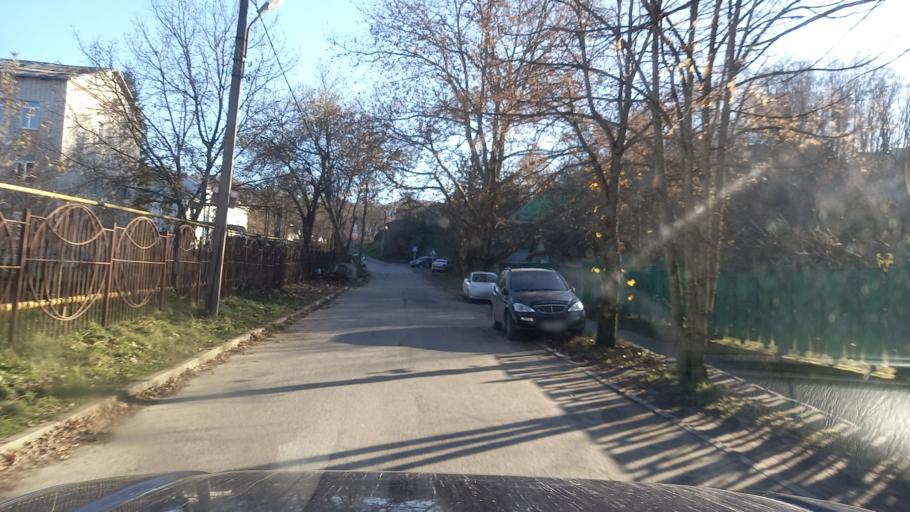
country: RU
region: Krasnodarskiy
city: Goryachiy Klyuch
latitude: 44.6262
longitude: 39.1056
